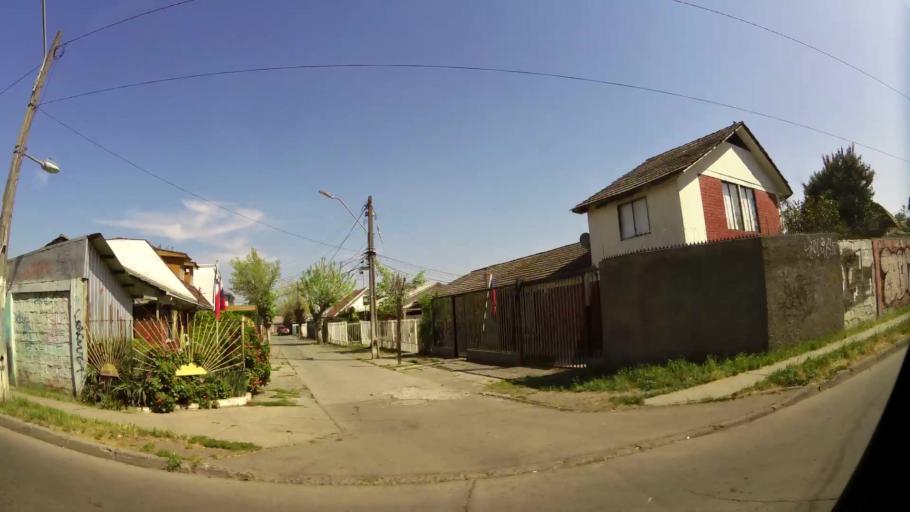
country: CL
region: Santiago Metropolitan
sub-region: Provincia de Santiago
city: Lo Prado
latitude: -33.4664
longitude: -70.7059
